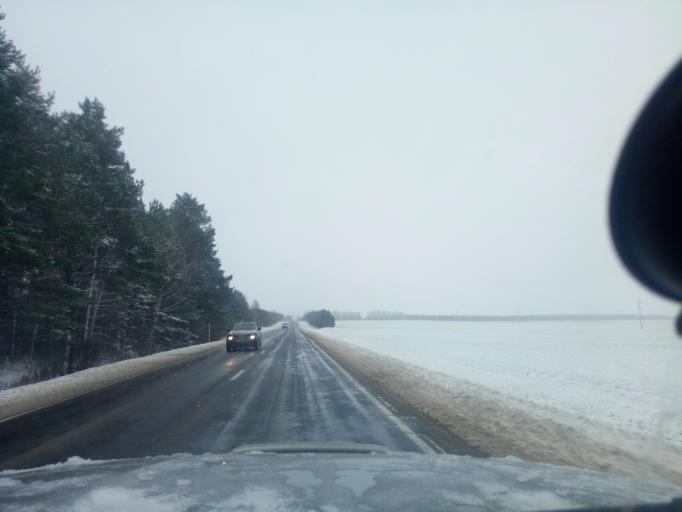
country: BY
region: Minsk
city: Haradzyeya
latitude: 53.3699
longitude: 26.5112
